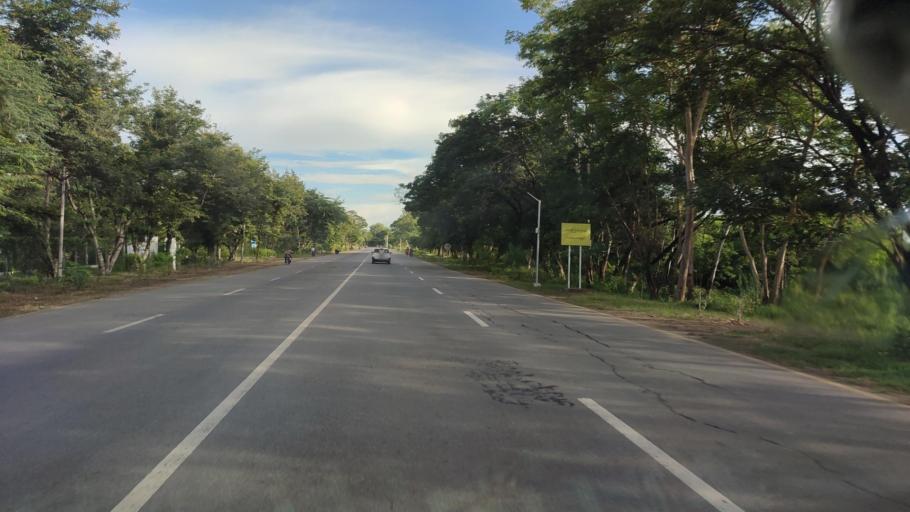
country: MM
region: Mandalay
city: Yamethin
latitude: 20.1491
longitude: 96.1928
